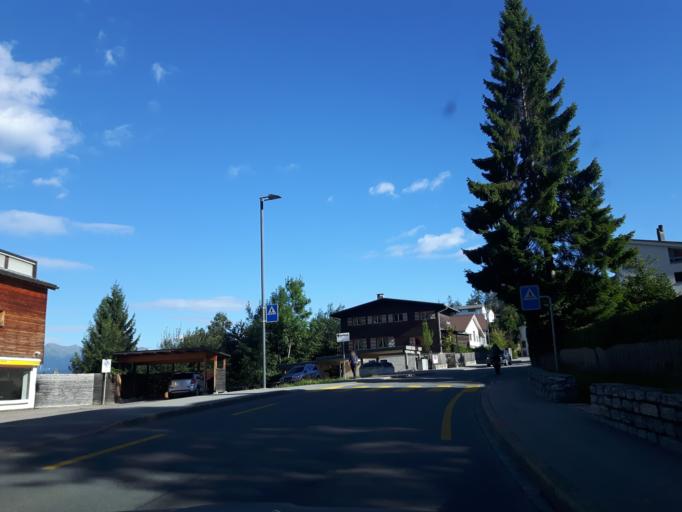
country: CH
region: Grisons
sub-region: Imboden District
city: Flims
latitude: 46.8313
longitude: 9.2847
